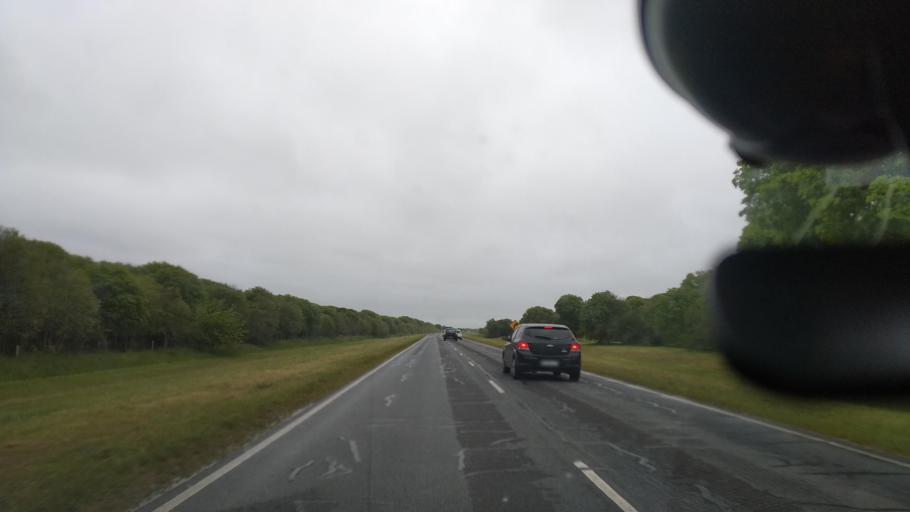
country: AR
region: Buenos Aires
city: Veronica
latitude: -35.7913
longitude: -57.4036
